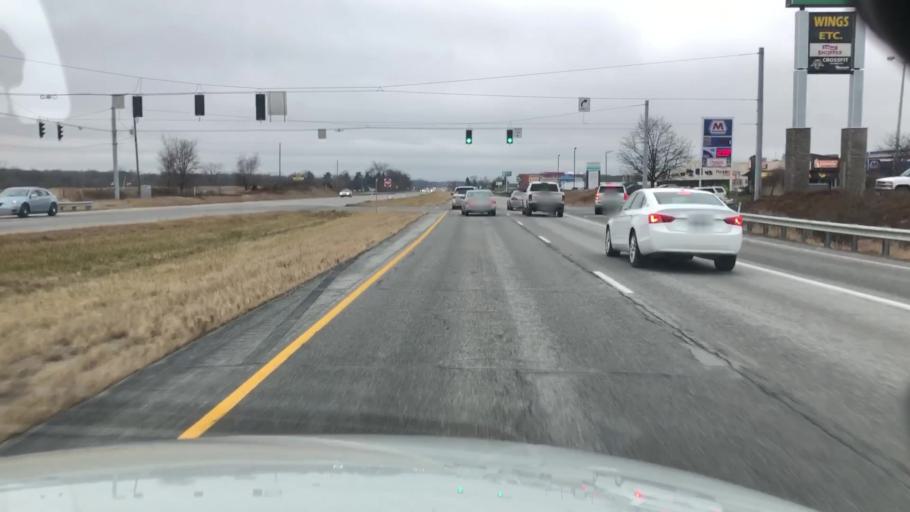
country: US
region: Indiana
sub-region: Whitley County
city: Columbia City
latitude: 41.1695
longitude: -85.5004
